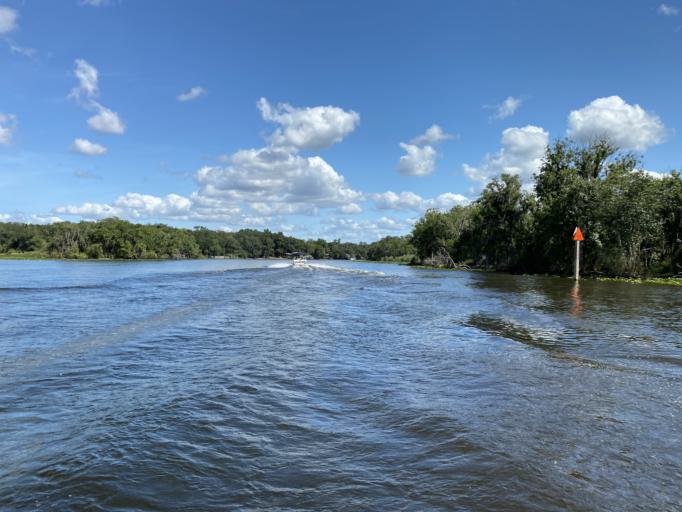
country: US
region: Florida
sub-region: Volusia County
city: DeBary
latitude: 28.8981
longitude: -81.3565
